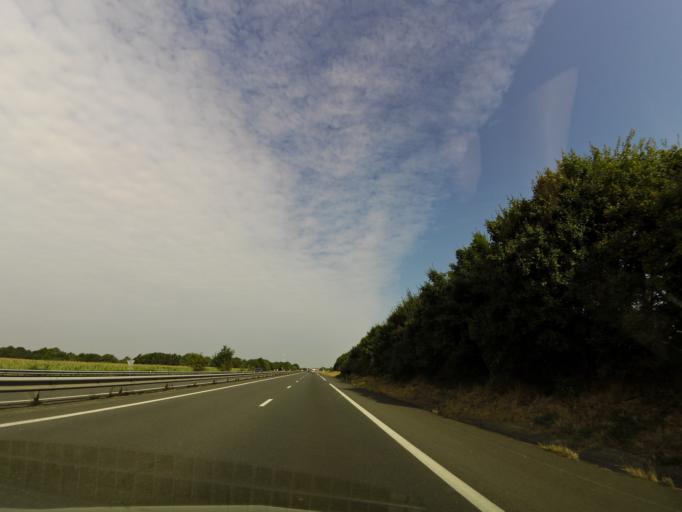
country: FR
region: Pays de la Loire
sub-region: Departement de la Loire-Atlantique
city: La Planche
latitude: 47.0191
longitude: -1.3957
